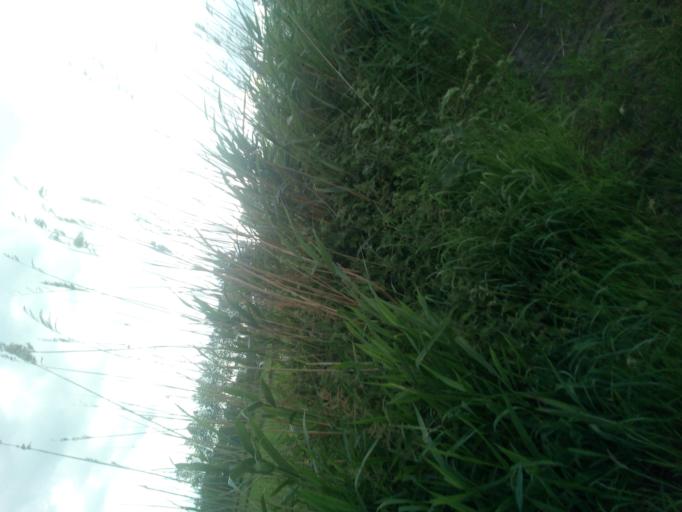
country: BE
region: Flanders
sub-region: Provincie West-Vlaanderen
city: Sint-Kruis
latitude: 51.1816
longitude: 3.2935
